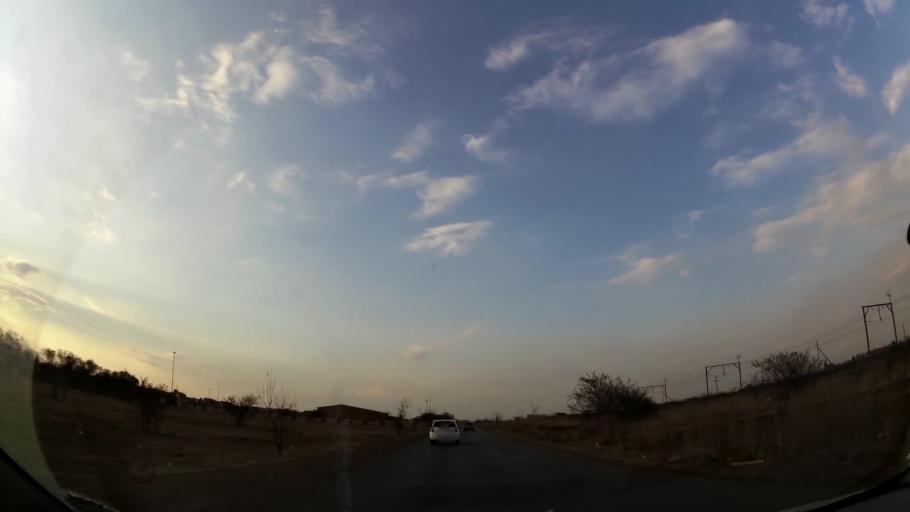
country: ZA
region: Gauteng
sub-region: City of Johannesburg Metropolitan Municipality
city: Orange Farm
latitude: -26.5692
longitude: 27.8606
